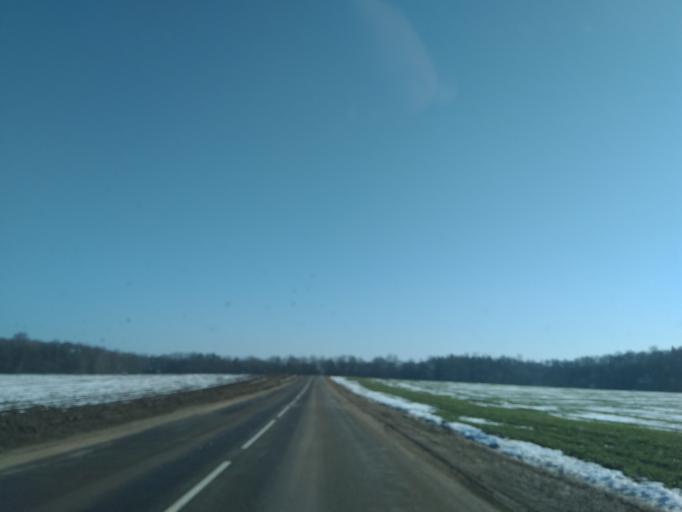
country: BY
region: Minsk
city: Nyasvizh
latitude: 53.2027
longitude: 26.6493
